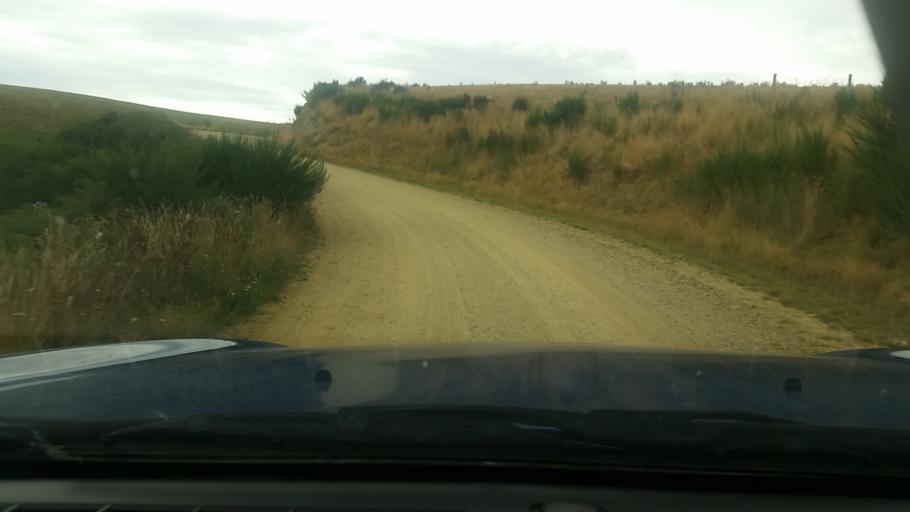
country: NZ
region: Otago
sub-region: Clutha District
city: Balclutha
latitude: -45.7031
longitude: 169.4818
